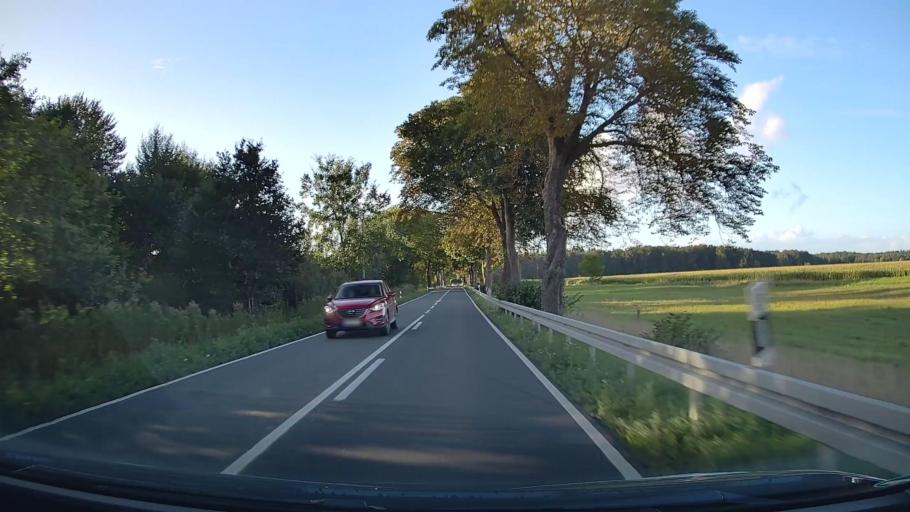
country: DE
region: Mecklenburg-Vorpommern
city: Steinhagen
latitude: 54.1954
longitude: 13.0156
